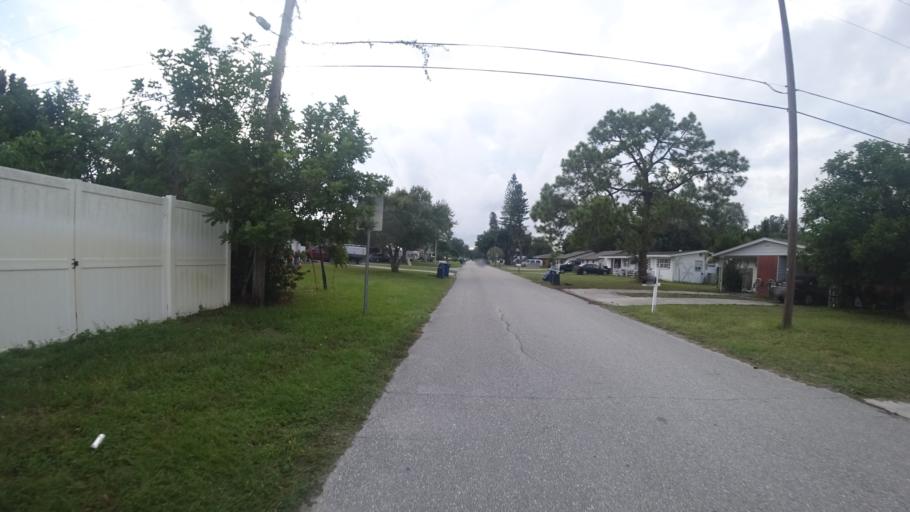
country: US
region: Florida
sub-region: Manatee County
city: South Bradenton
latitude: 27.4570
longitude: -82.5834
